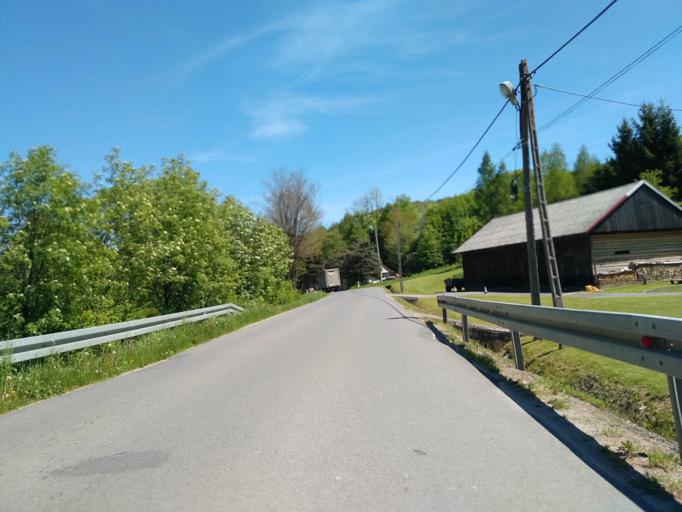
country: PL
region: Subcarpathian Voivodeship
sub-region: Powiat sanocki
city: Bukowsko
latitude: 49.5211
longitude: 22.0360
